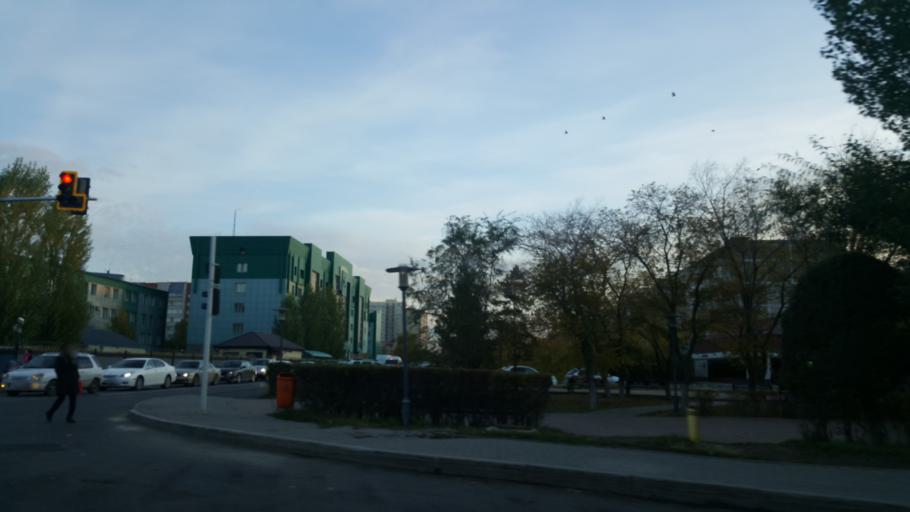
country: KZ
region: Astana Qalasy
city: Astana
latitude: 51.1515
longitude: 71.4943
